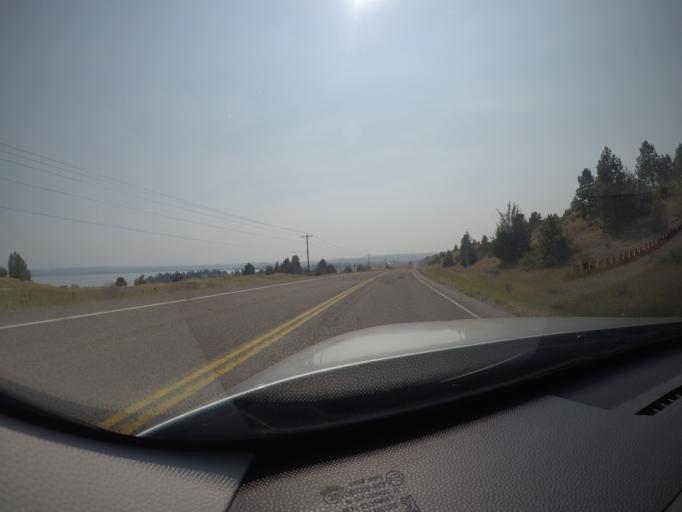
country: US
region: Montana
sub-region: Lake County
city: Polson
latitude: 47.7442
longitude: -114.1742
